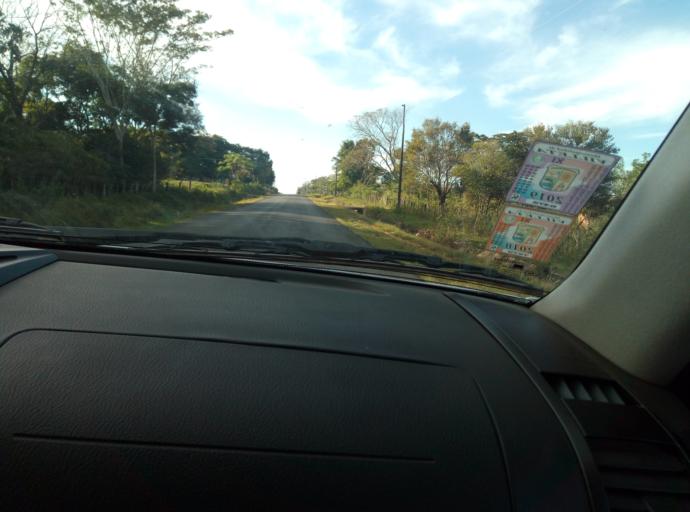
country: PY
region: Caaguazu
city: Carayao
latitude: -25.1632
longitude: -56.3124
